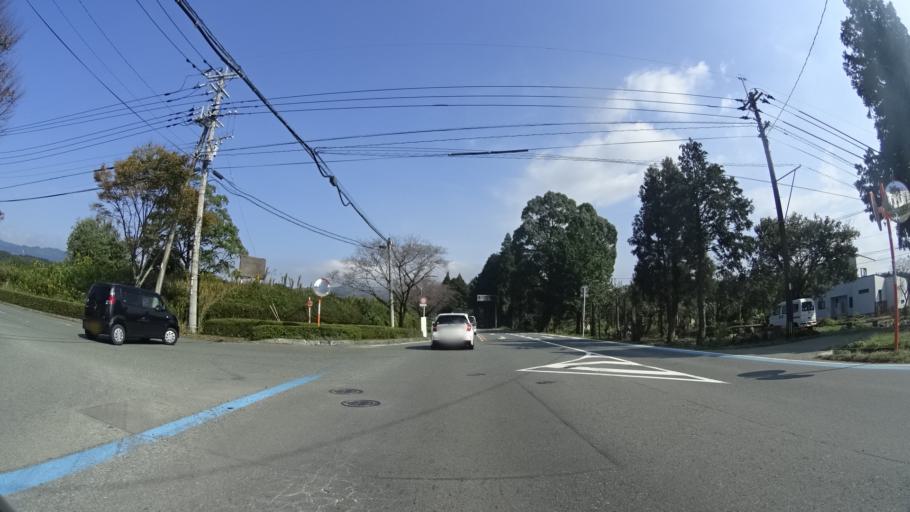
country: JP
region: Kumamoto
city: Ozu
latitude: 32.8939
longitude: 130.9185
